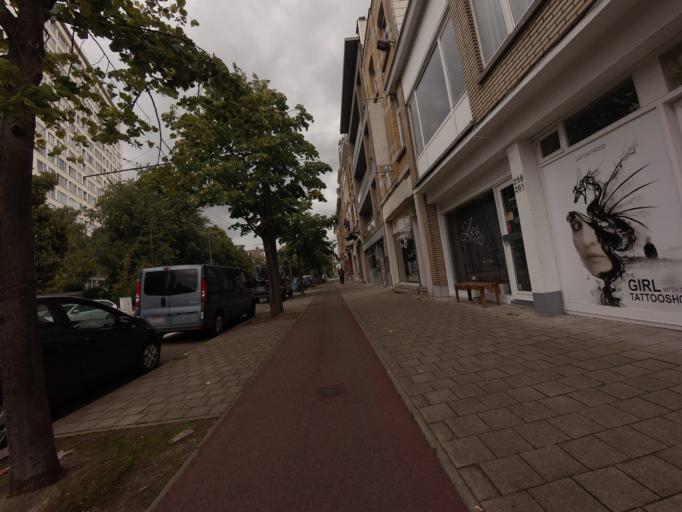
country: BE
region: Flanders
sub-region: Provincie Antwerpen
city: Antwerpen
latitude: 51.1824
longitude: 4.3931
